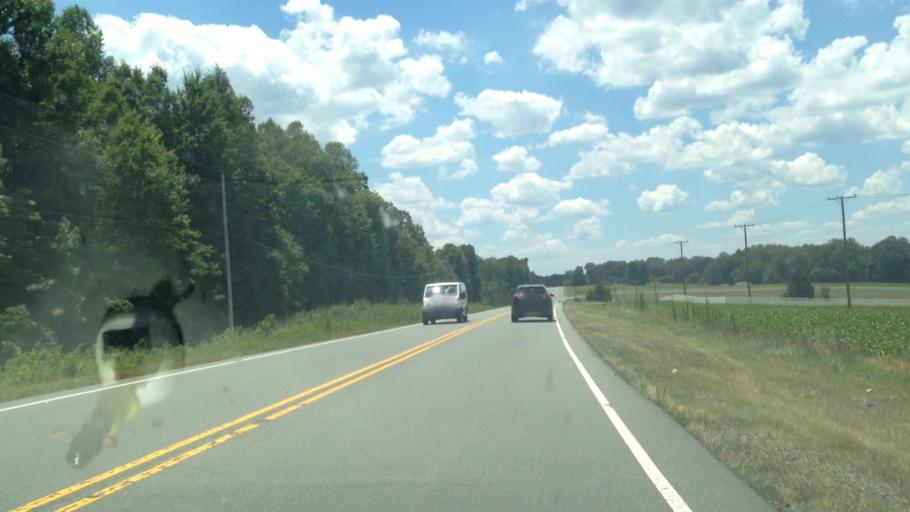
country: US
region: North Carolina
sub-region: Forsyth County
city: Walkertown
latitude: 36.1954
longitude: -80.0930
